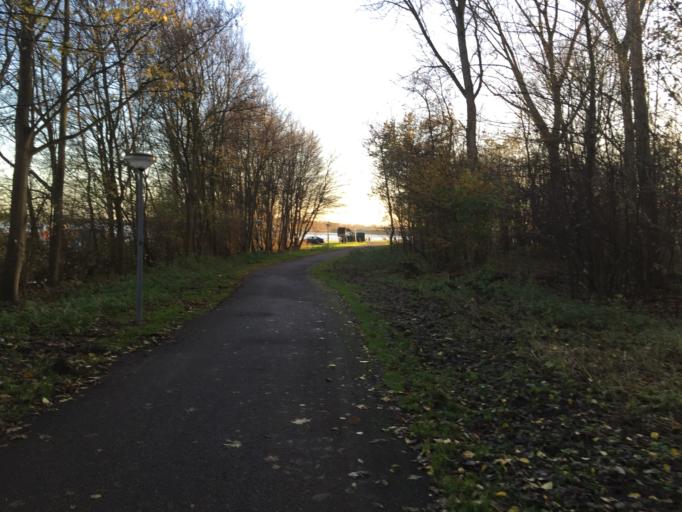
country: NL
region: South Holland
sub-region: Gemeente Albrandswaard
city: Rhoon
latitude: 51.8432
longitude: 4.4224
